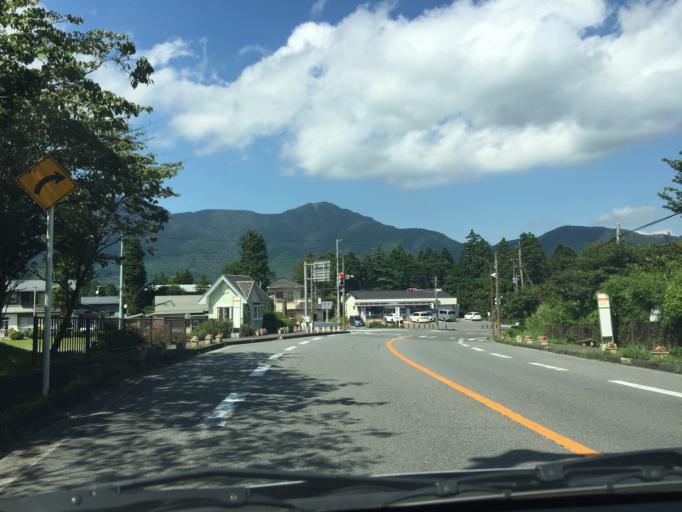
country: JP
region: Shizuoka
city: Gotemba
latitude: 35.2585
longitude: 139.0008
